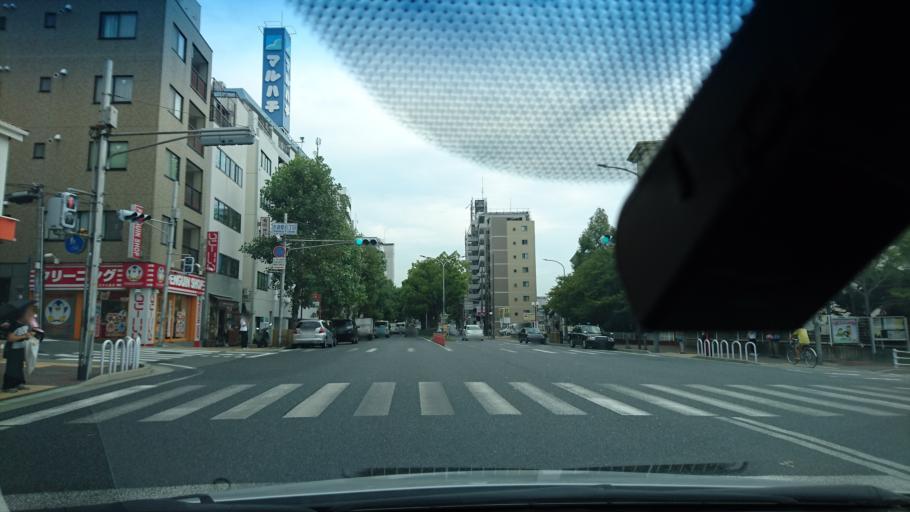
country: JP
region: Hyogo
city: Kobe
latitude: 34.7112
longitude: 135.2215
